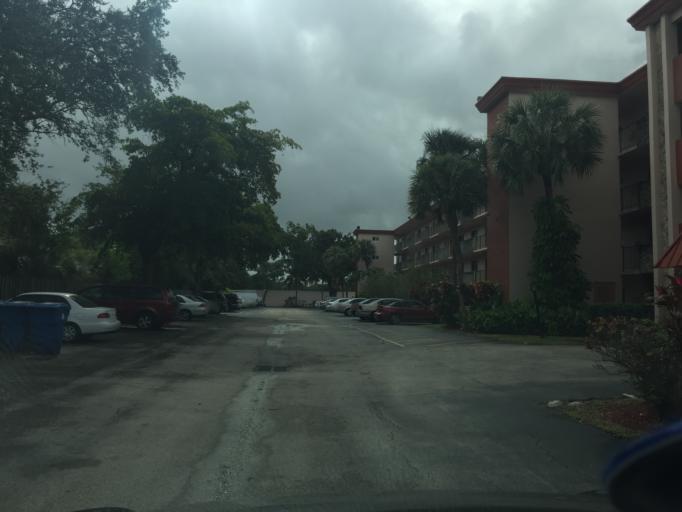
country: US
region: Florida
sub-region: Broward County
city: Plantation
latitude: 26.1364
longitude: -80.2262
